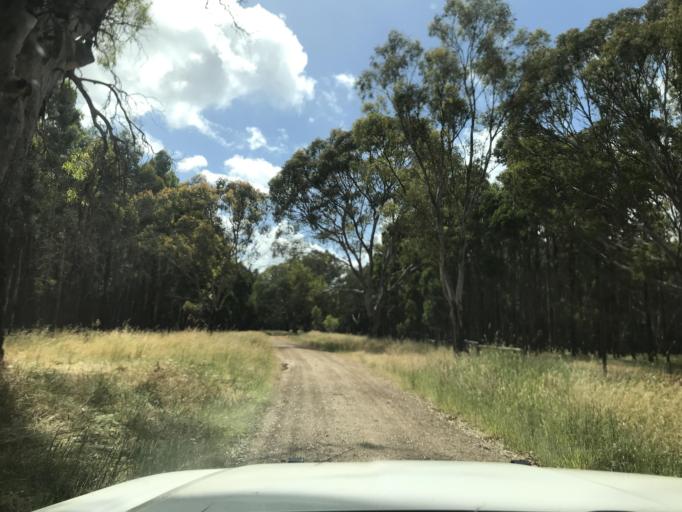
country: AU
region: South Australia
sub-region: Wattle Range
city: Penola
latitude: -37.1897
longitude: 141.3760
